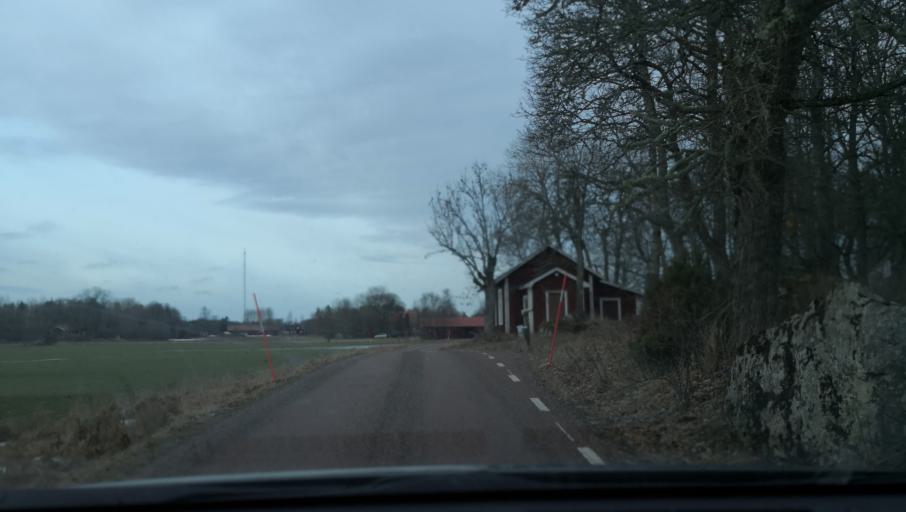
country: SE
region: Vaestmanland
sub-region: Vasteras
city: Skultuna
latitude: 59.6192
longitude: 16.4122
